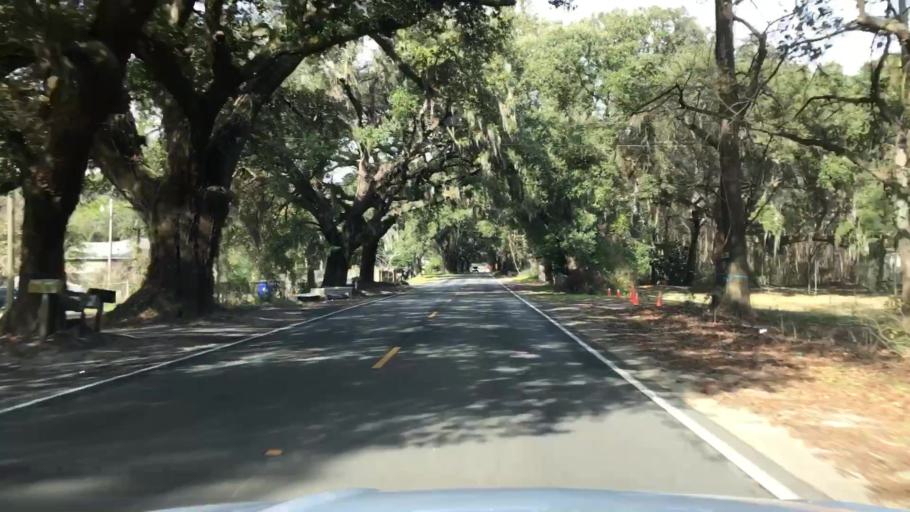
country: US
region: South Carolina
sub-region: Charleston County
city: Shell Point
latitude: 32.7365
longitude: -80.0330
